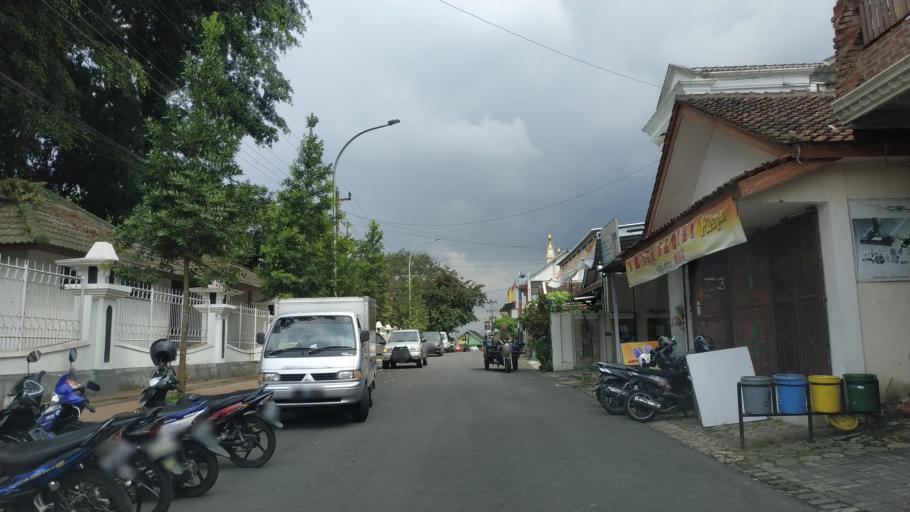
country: ID
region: Central Java
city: Magelang
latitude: -7.3146
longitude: 110.1750
